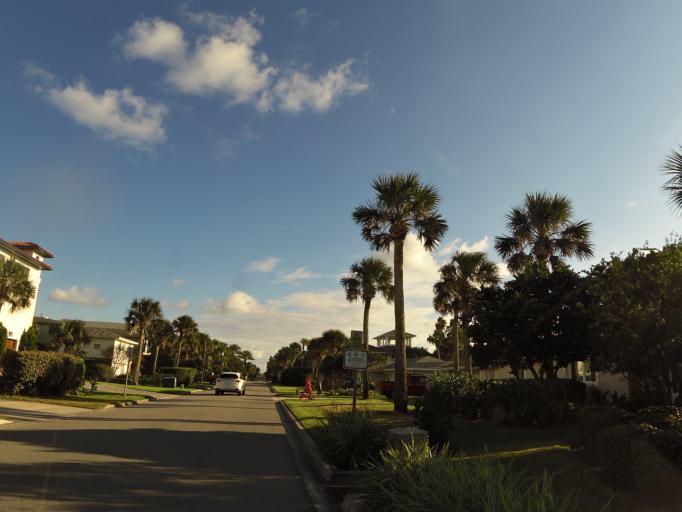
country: US
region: Florida
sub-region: Saint Johns County
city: Ponte Vedra Beach
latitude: 30.2602
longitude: -81.3833
